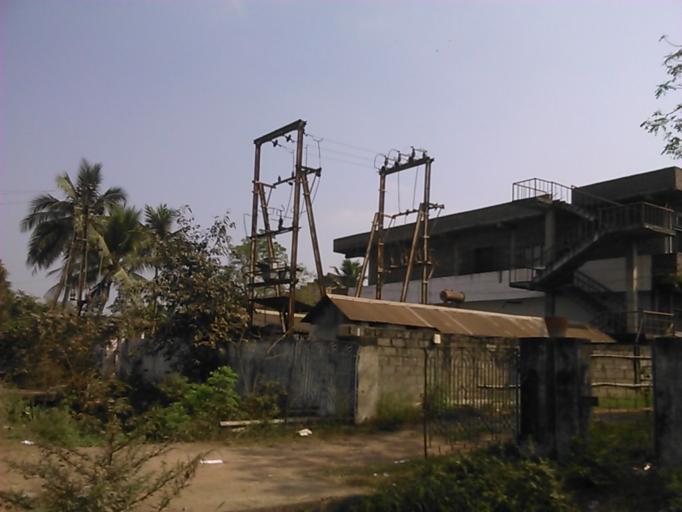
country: IN
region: Andhra Pradesh
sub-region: Guntur
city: Bhattiprolu
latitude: 16.2374
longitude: 80.6668
